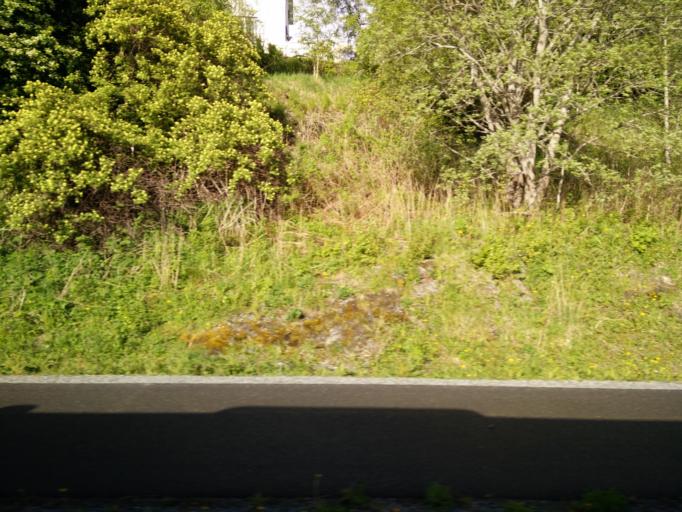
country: NO
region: Sor-Trondelag
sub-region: Skaun
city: Borsa
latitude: 63.3176
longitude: 10.1506
